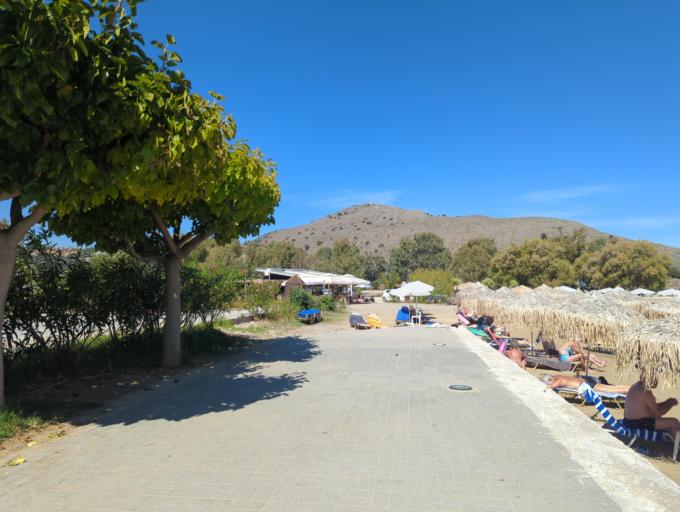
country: GR
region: Crete
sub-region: Nomos Chanias
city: Georgioupolis
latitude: 35.3639
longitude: 24.2618
